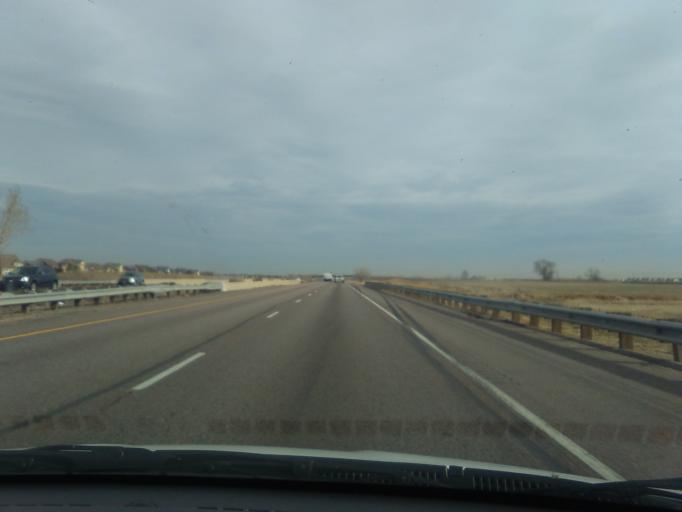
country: US
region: Colorado
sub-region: Adams County
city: Derby
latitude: 39.8913
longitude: -104.8571
